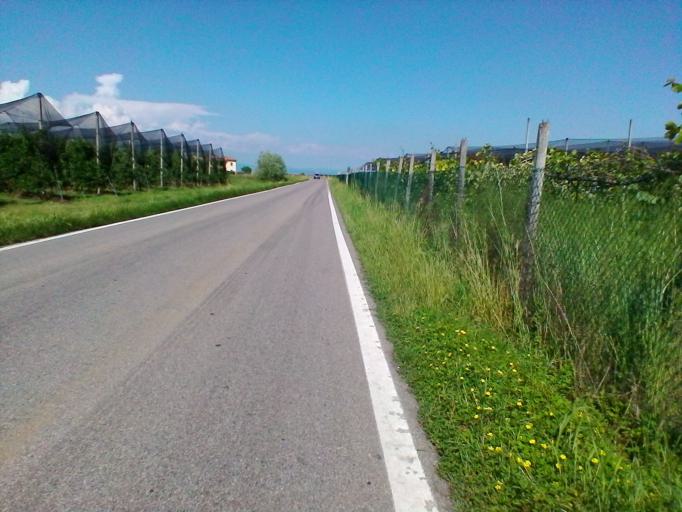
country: IT
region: Veneto
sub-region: Provincia di Verona
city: Povegliano Veronese
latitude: 45.3582
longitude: 10.8881
